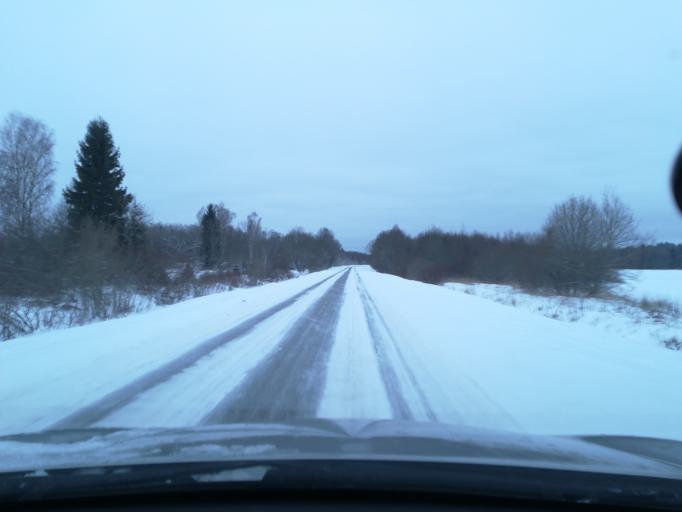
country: EE
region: Harju
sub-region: Keila linn
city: Keila
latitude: 59.3770
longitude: 24.3072
